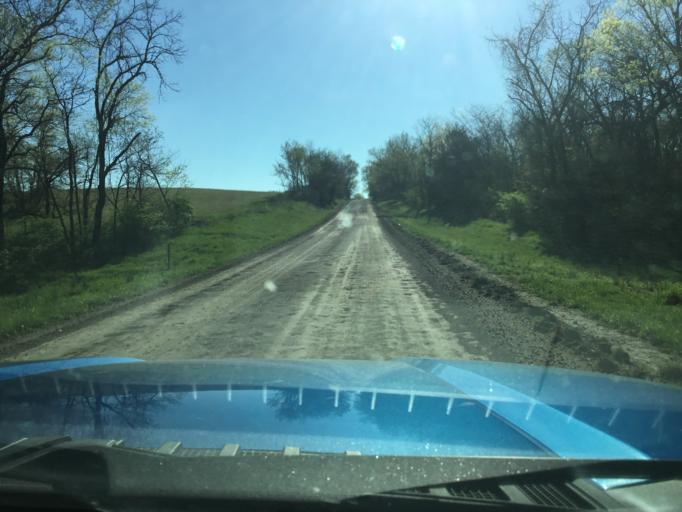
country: US
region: Kansas
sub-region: Douglas County
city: Lawrence
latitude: 38.9569
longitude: -95.3627
